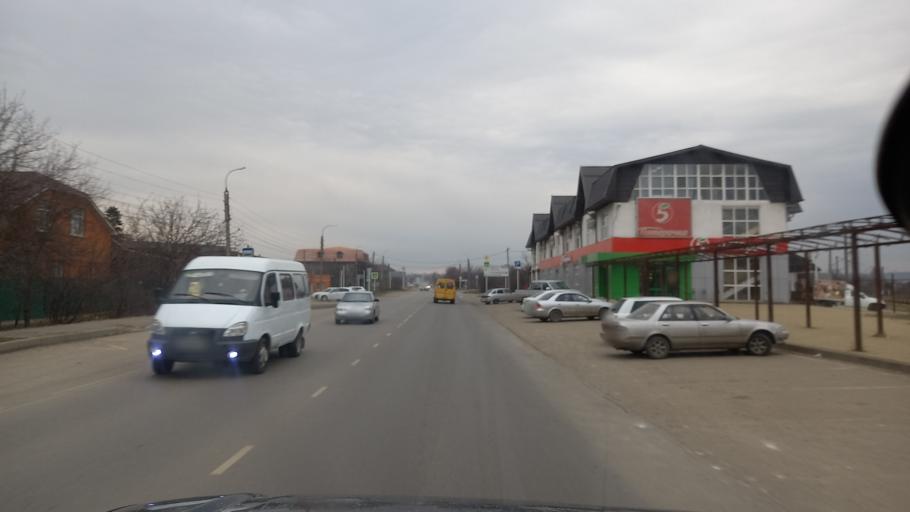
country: RU
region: Adygeya
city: Maykop
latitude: 44.5866
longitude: 40.1326
